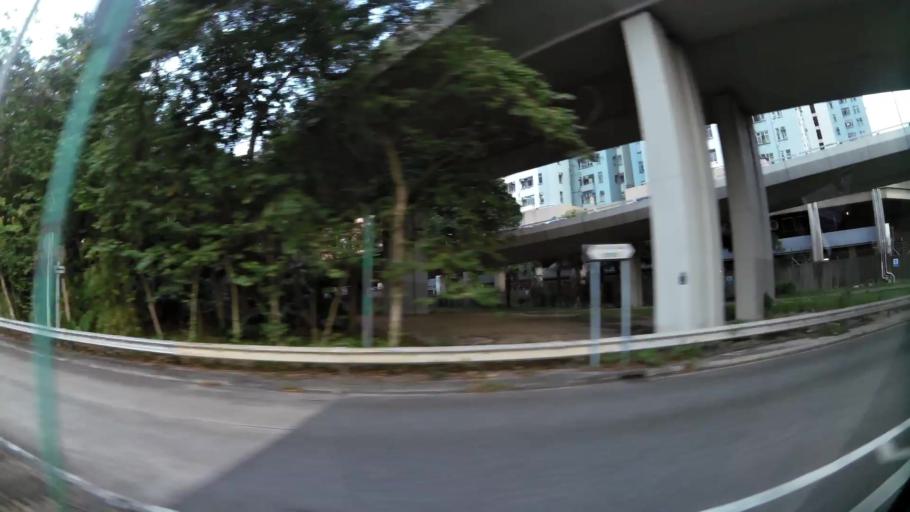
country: HK
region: Kowloon City
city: Kowloon
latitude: 22.3259
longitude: 114.2116
